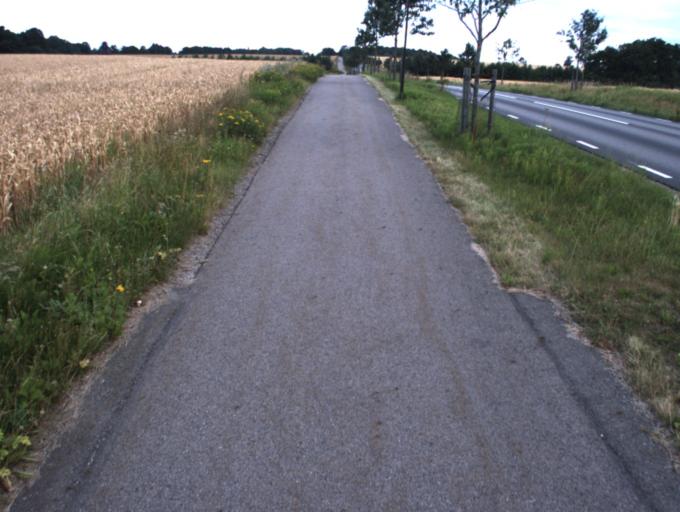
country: SE
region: Skane
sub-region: Helsingborg
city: Helsingborg
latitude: 56.1003
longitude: 12.6481
